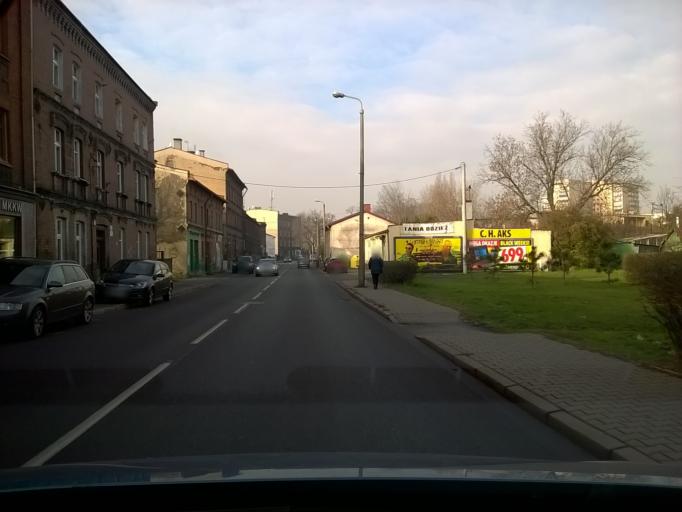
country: PL
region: Silesian Voivodeship
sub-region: Chorzow
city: Chorzow
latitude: 50.2824
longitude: 18.9548
